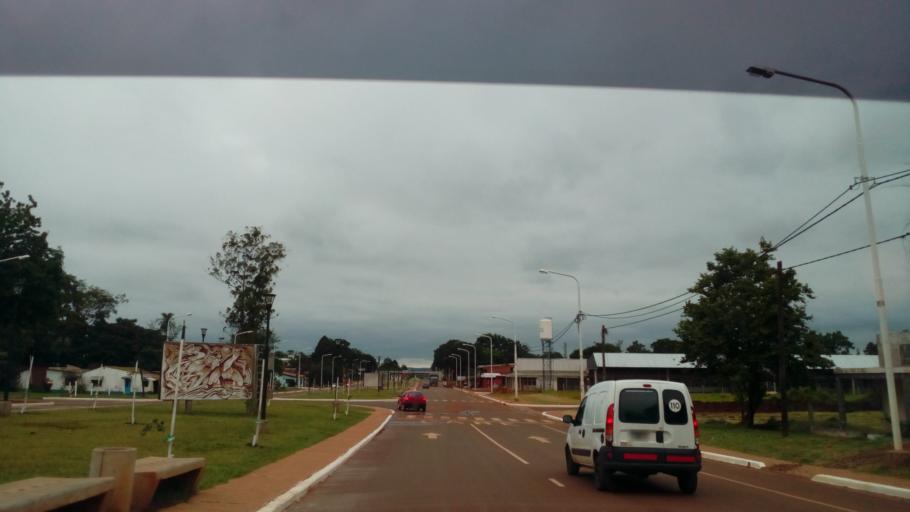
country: AR
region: Misiones
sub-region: Departamento de Candelaria
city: Candelaria
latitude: -27.4656
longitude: -55.7454
